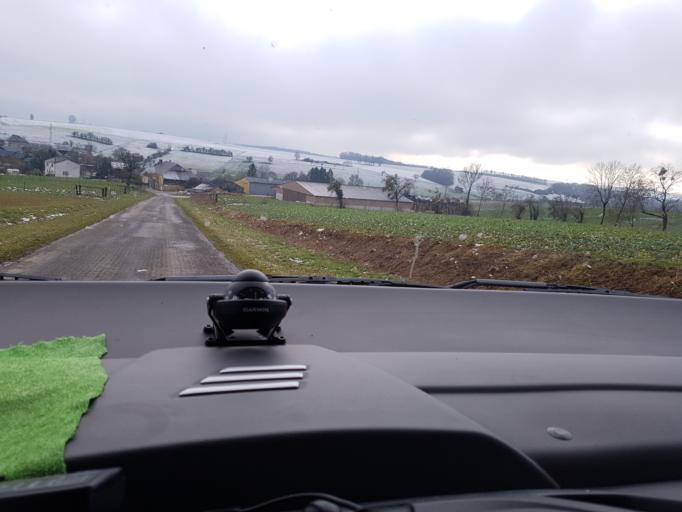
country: FR
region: Champagne-Ardenne
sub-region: Departement des Ardennes
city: Rimogne
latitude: 49.8224
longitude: 4.3999
